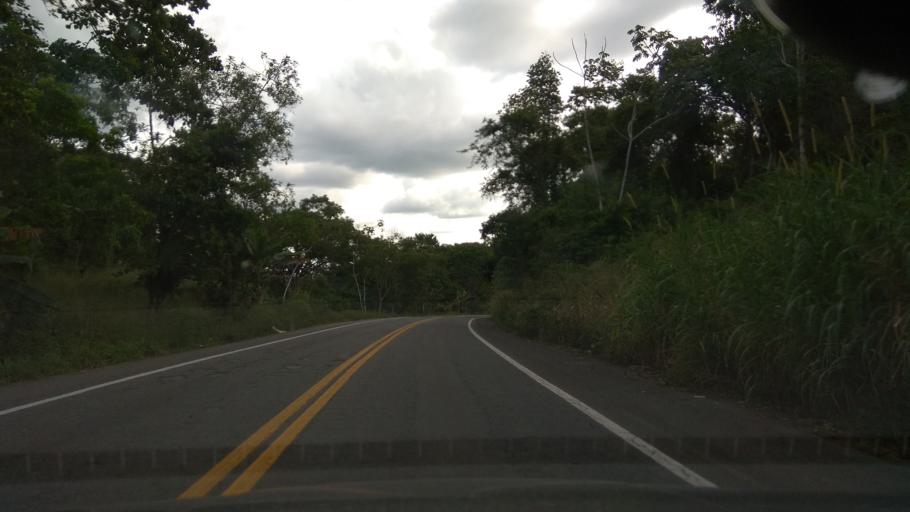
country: BR
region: Bahia
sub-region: Ubaitaba
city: Ubaitaba
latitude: -14.2624
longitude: -39.3372
